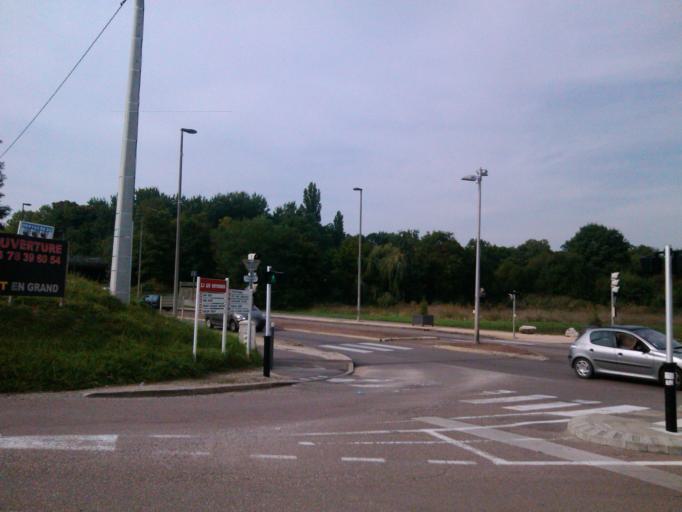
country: FR
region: Bourgogne
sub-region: Departement de Saone-et-Loire
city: Chatenoy-le-Royal
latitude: 46.7933
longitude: 4.8237
